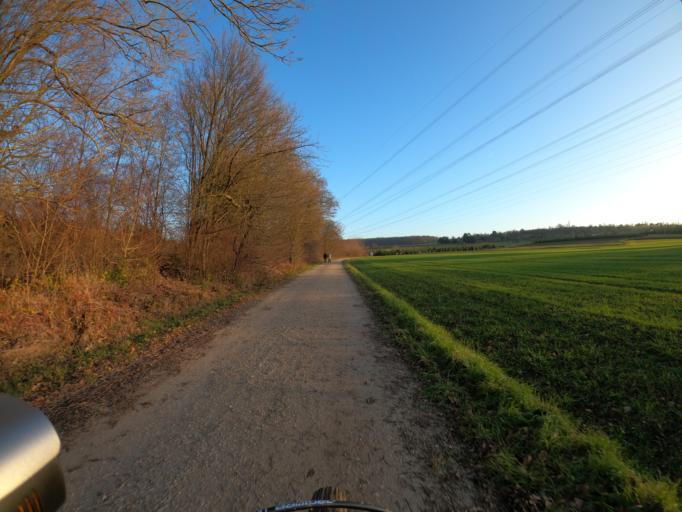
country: DE
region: Baden-Wuerttemberg
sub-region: Regierungsbezirk Stuttgart
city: Notzingen
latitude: 48.6720
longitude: 9.4366
